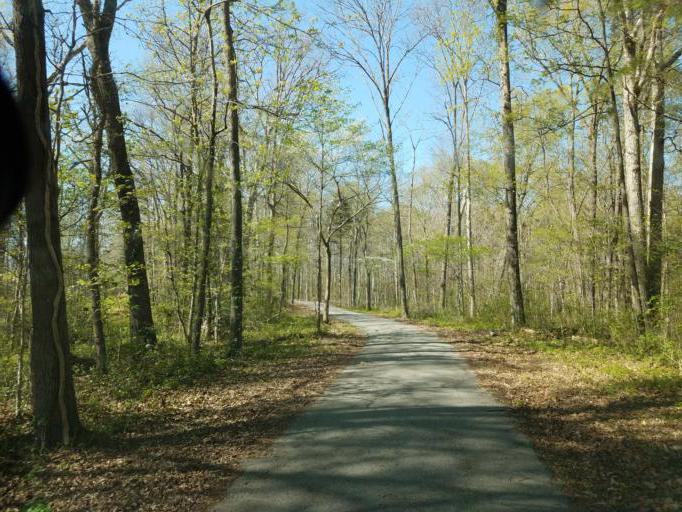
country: US
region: Kentucky
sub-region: Edmonson County
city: Brownsville
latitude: 37.1311
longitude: -86.1469
